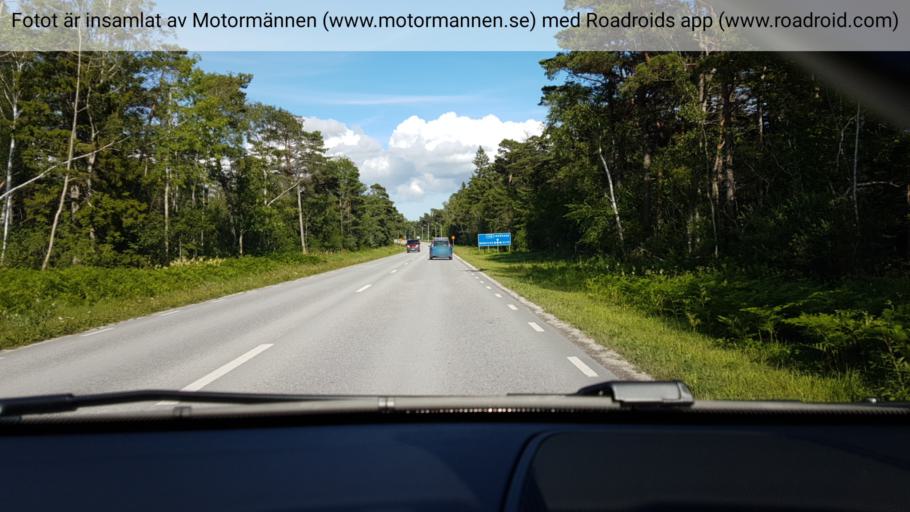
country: SE
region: Gotland
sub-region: Gotland
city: Slite
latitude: 57.7493
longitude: 18.7242
